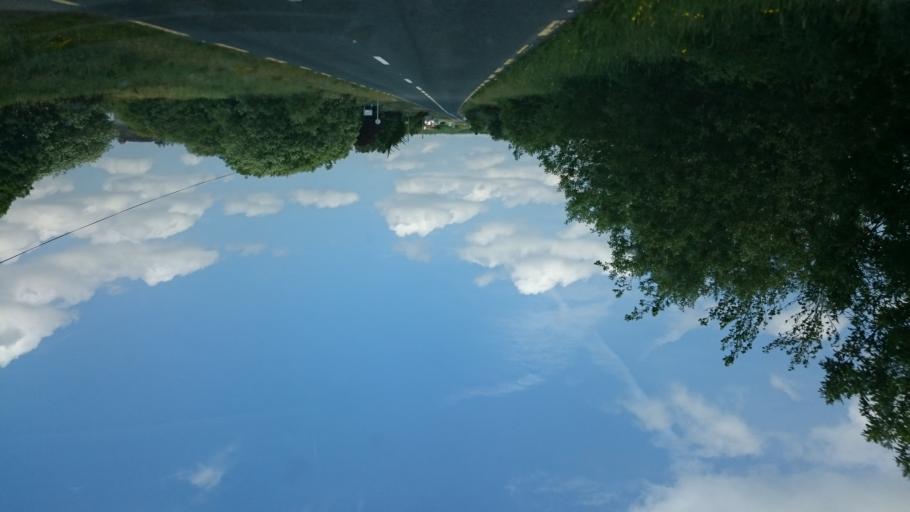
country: IE
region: Connaught
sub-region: Maigh Eo
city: Ballyhaunis
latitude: 53.8840
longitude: -8.7951
